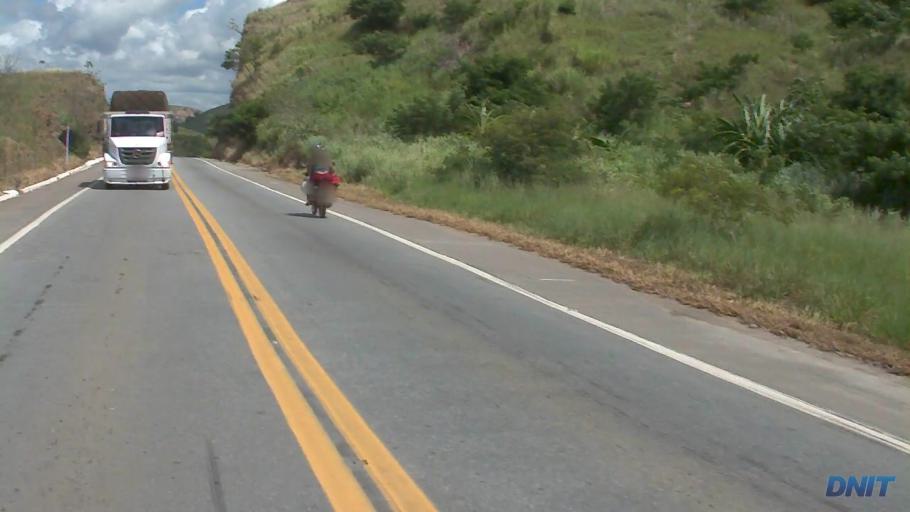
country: BR
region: Minas Gerais
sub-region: Governador Valadares
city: Governador Valadares
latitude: -18.9290
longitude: -42.0434
